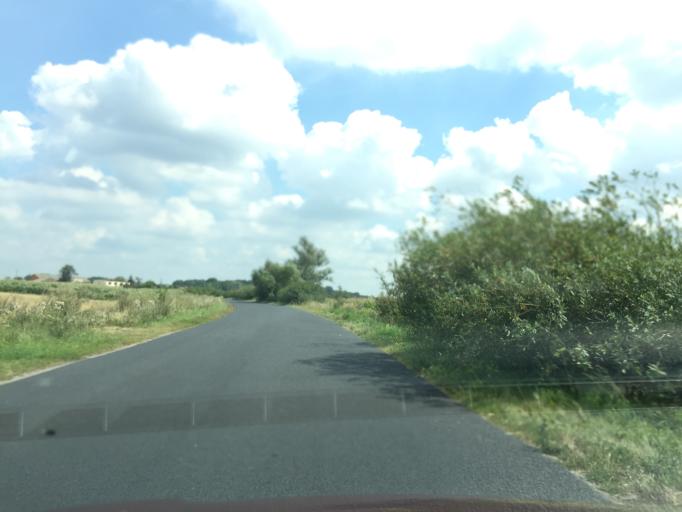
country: PL
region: Greater Poland Voivodeship
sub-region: Powiat kaliski
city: Stawiszyn
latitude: 51.9194
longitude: 18.1279
